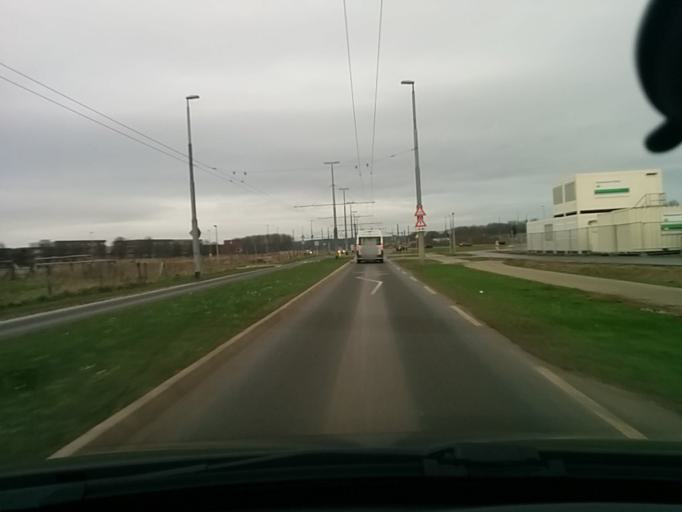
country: NL
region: Gelderland
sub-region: Gemeente Renkum
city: Oosterbeek
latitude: 51.9536
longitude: 5.8462
